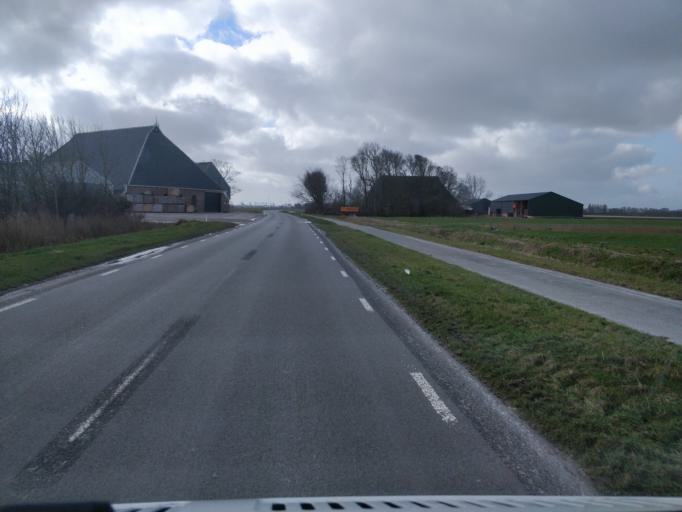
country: NL
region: Friesland
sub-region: Gemeente Franekeradeel
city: Sexbierum
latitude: 53.2084
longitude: 5.4633
